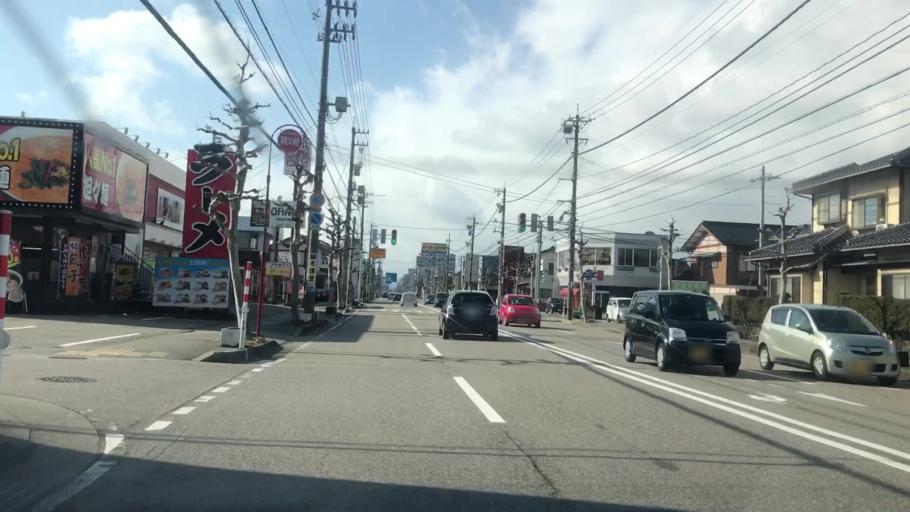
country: JP
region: Toyama
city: Takaoka
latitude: 36.7387
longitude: 137.0247
